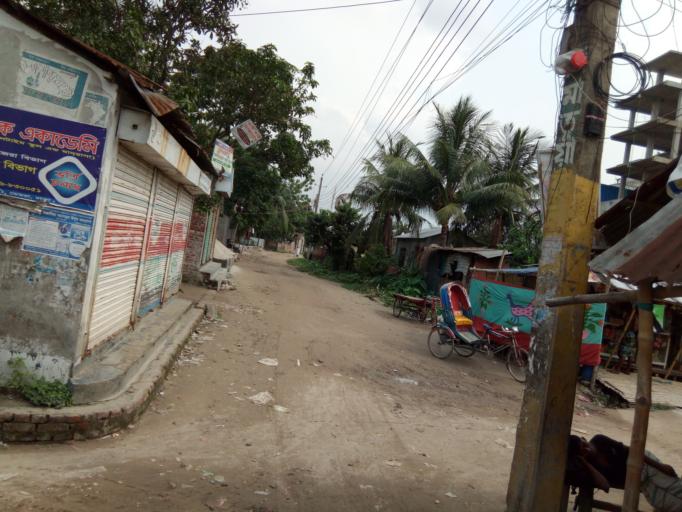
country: BD
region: Dhaka
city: Paltan
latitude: 23.7080
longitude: 90.4784
